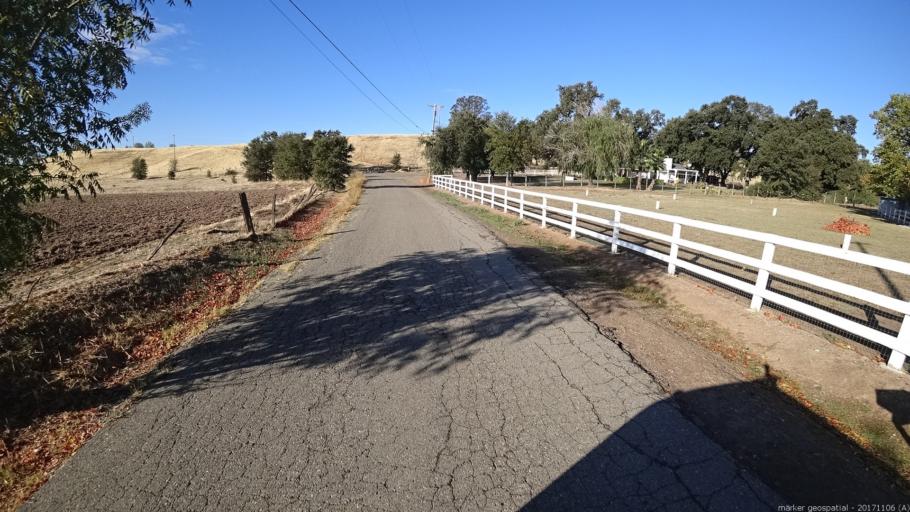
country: US
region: California
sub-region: Shasta County
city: Anderson
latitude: 40.4914
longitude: -122.2406
